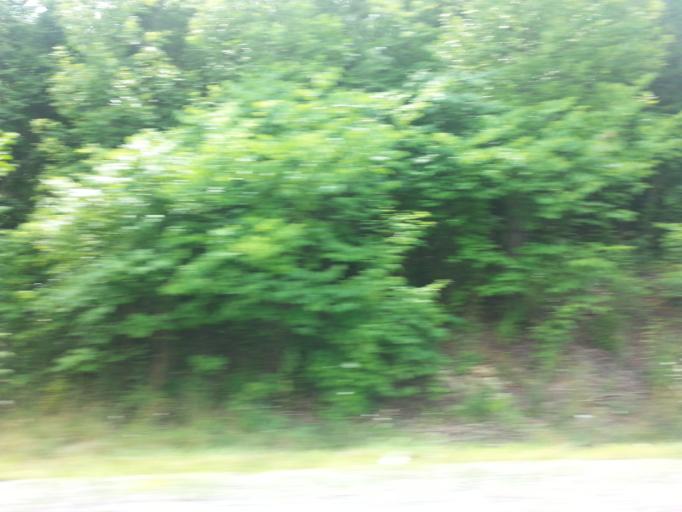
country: US
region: Tennessee
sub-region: Putnam County
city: Monterey
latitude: 36.1403
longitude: -85.3650
